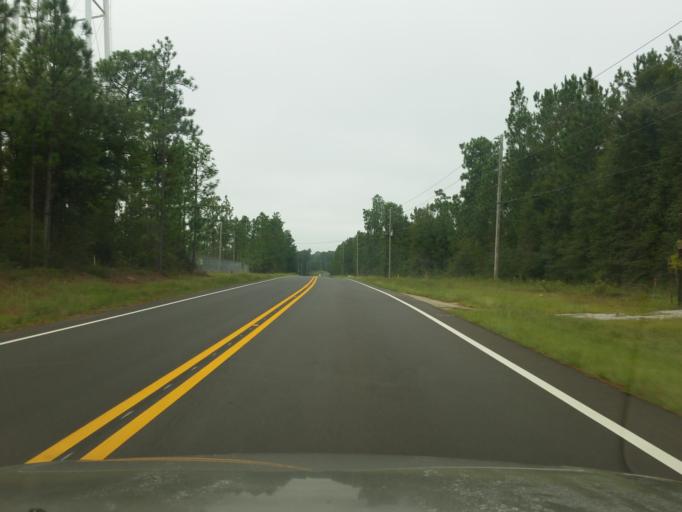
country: US
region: Alabama
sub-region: Baldwin County
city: Spanish Fort
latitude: 30.7916
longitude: -87.8758
